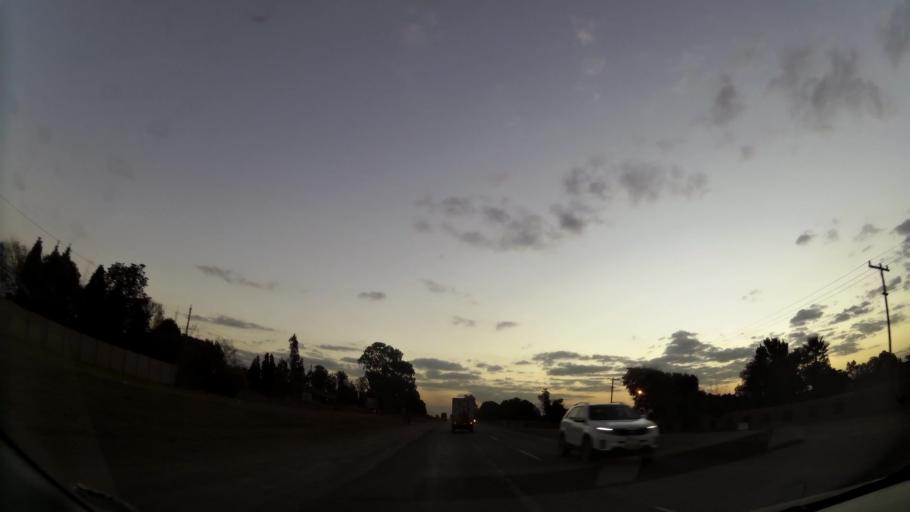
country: ZA
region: Gauteng
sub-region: West Rand District Municipality
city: Krugersdorp
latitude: -26.0699
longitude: 27.6779
